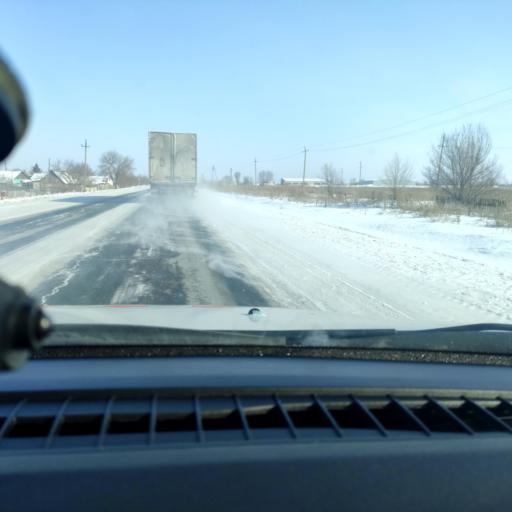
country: RU
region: Samara
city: Smyshlyayevka
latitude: 53.1810
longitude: 50.4660
